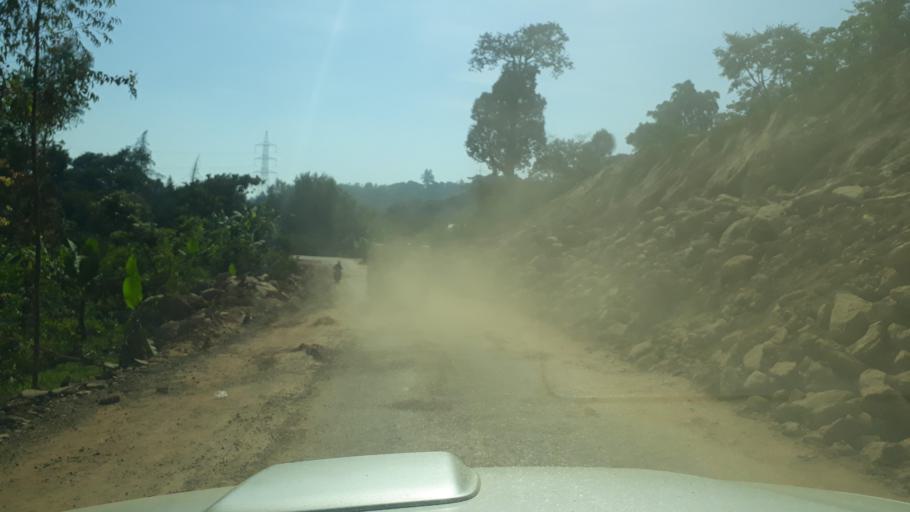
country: ET
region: Oromiya
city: Agaro
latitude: 7.8075
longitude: 36.6923
